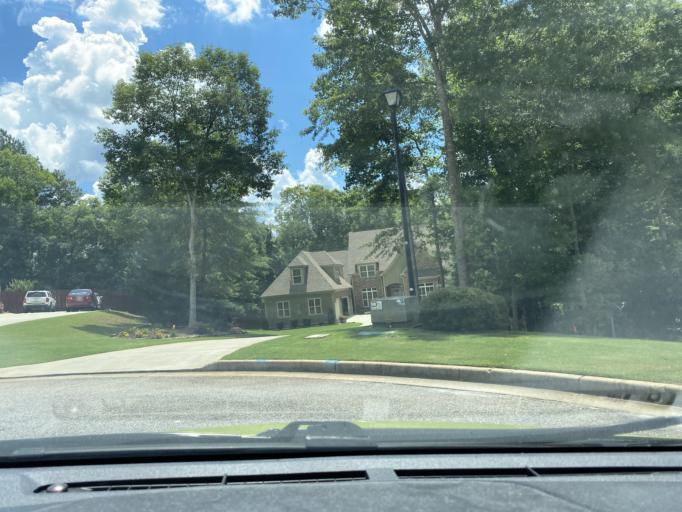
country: US
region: Georgia
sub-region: Fayette County
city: Peachtree City
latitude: 33.4254
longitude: -84.6715
